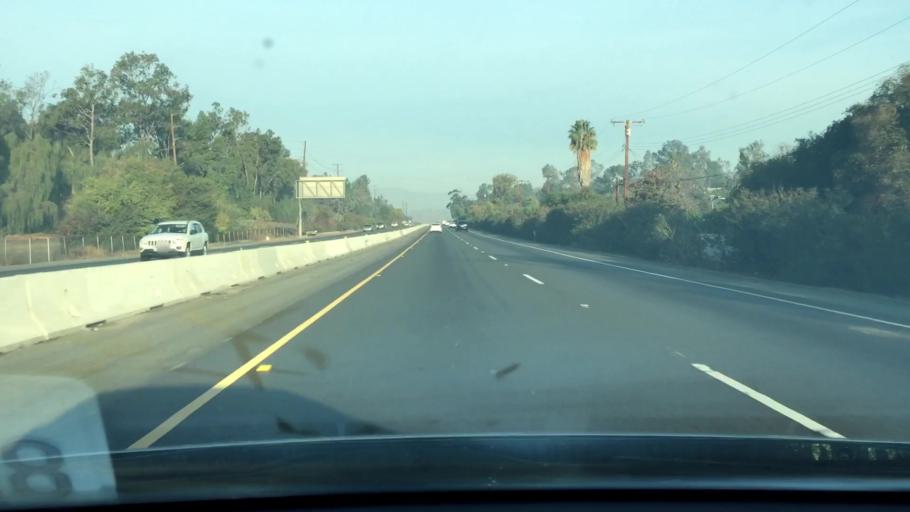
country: US
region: California
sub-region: Los Angeles County
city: Pomona
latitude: 34.0389
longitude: -117.7657
